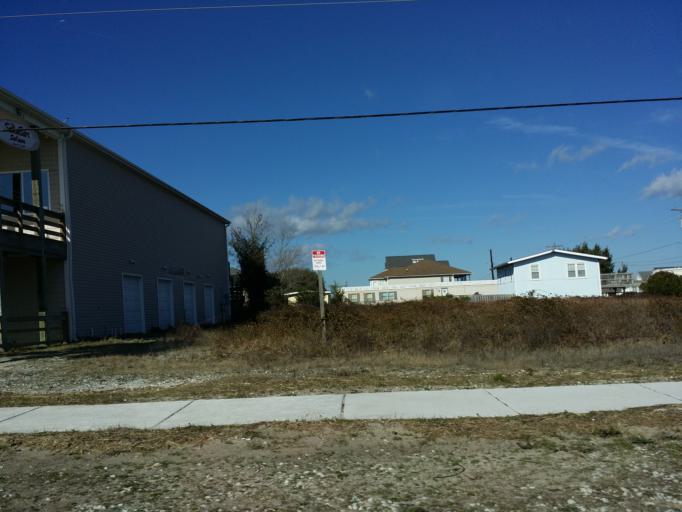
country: US
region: North Carolina
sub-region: Pender County
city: Surf City
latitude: 34.4429
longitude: -77.5180
